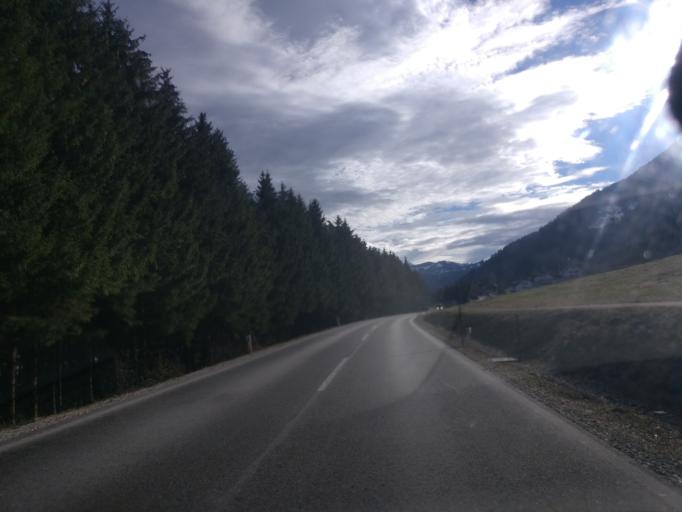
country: AT
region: Styria
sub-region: Politischer Bezirk Liezen
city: Ardning
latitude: 47.5797
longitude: 14.3236
